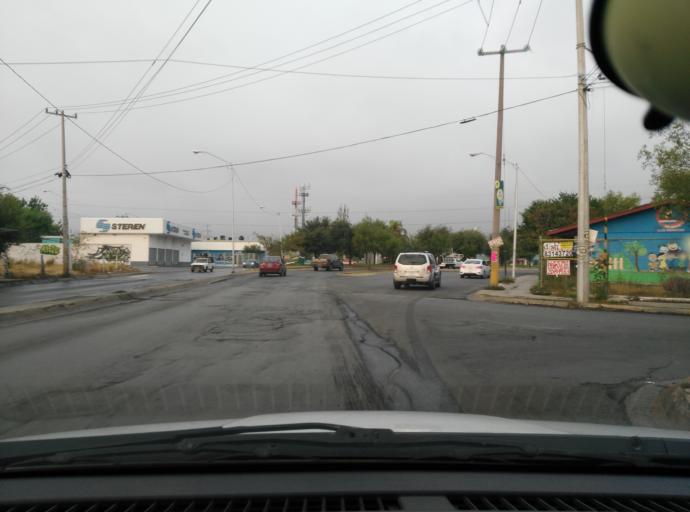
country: MX
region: Nuevo Leon
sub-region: San Nicolas de los Garza
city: San Nicolas de los Garza
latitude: 25.7716
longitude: -100.2619
